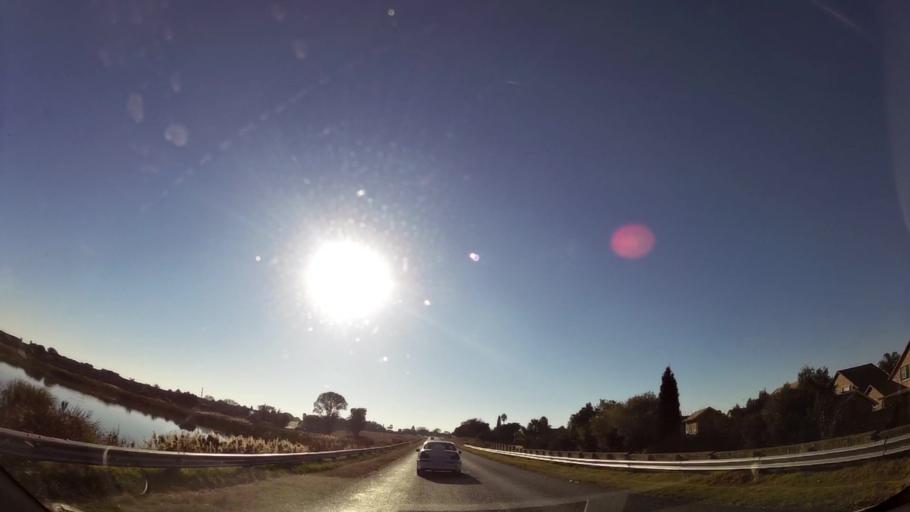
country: ZA
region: Gauteng
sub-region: City of Johannesburg Metropolitan Municipality
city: Modderfontein
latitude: -26.0671
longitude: 28.2168
